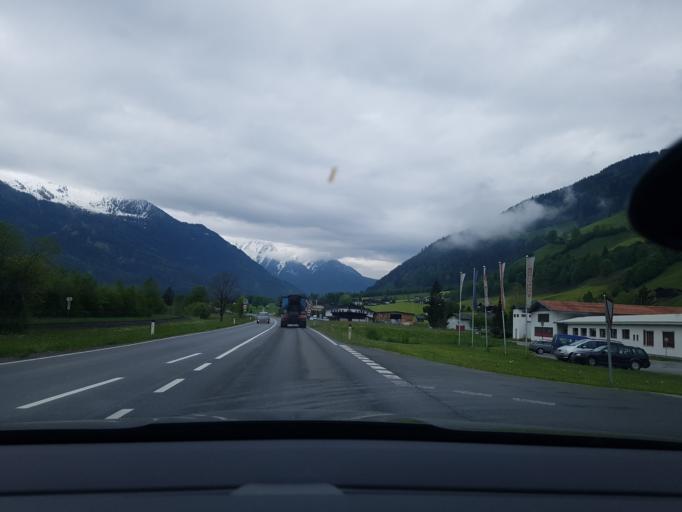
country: AT
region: Salzburg
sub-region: Politischer Bezirk Zell am See
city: Bramberg am Wildkogel
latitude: 47.2670
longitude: 12.3361
